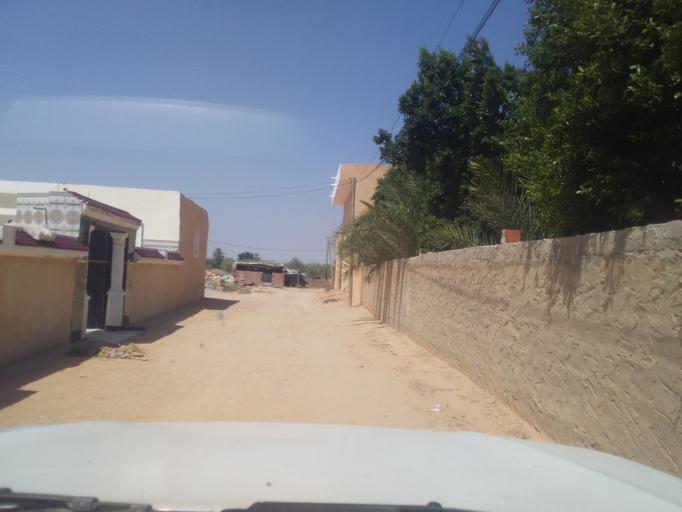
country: TN
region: Qabis
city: Matmata
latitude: 33.5917
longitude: 10.2835
